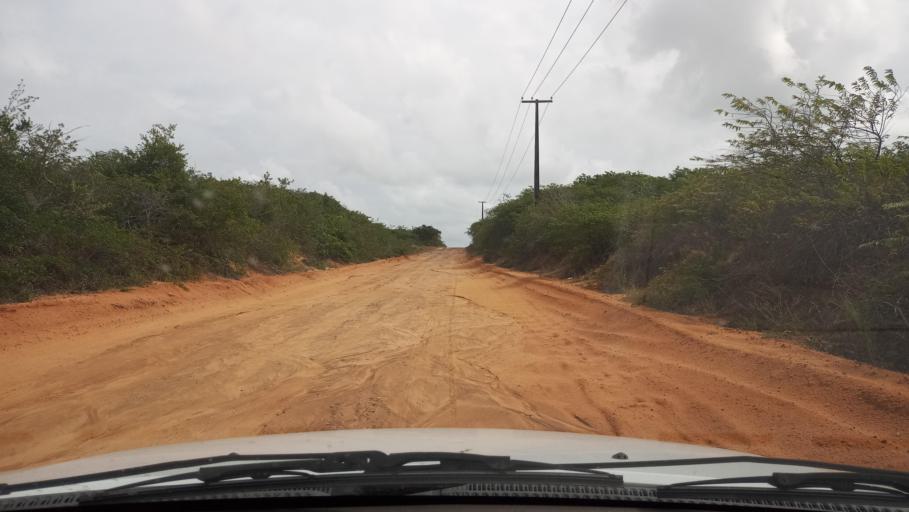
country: BR
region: Rio Grande do Norte
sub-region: Maxaranguape
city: Sao Miguel
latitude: -5.4818
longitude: -35.3034
